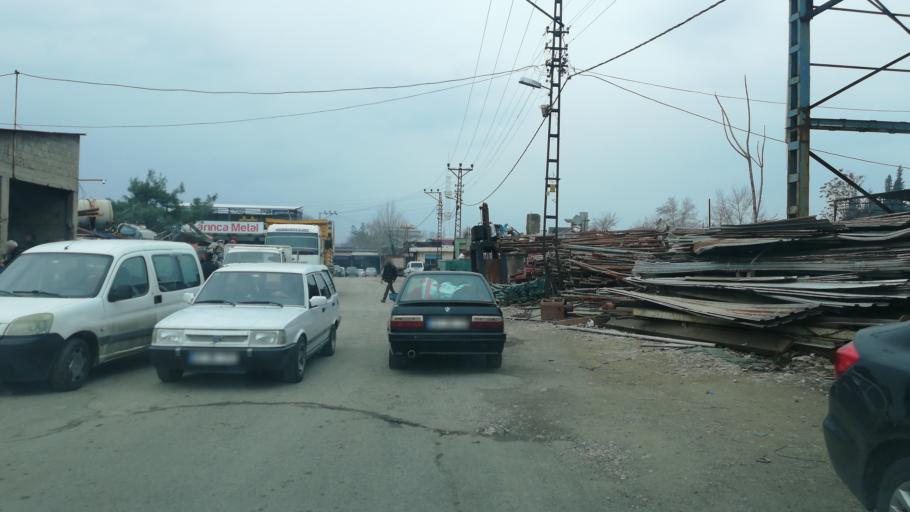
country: TR
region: Kahramanmaras
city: Kahramanmaras
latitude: 37.5666
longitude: 36.9562
